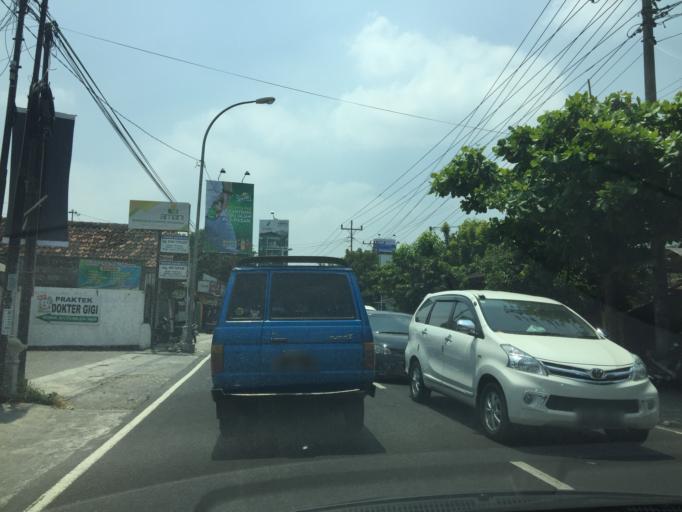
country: ID
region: Daerah Istimewa Yogyakarta
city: Melati
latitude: -7.7507
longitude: 110.3714
